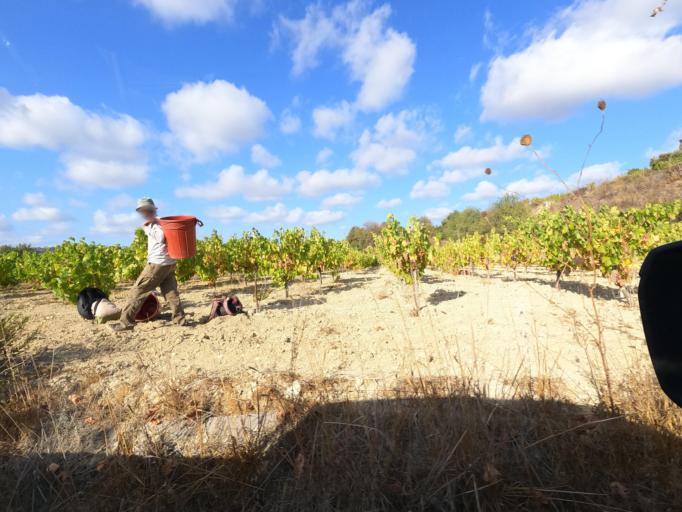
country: CY
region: Pafos
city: Mesogi
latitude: 34.8365
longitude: 32.5258
